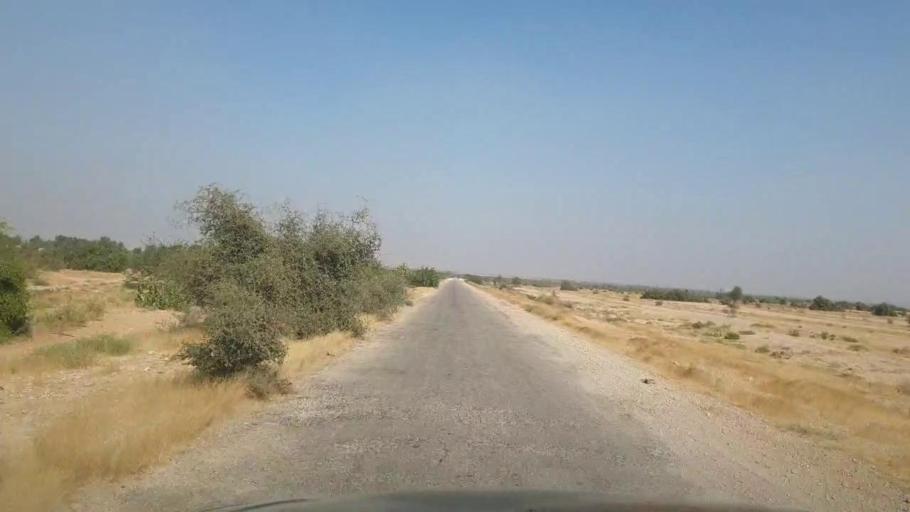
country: PK
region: Sindh
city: Jamshoro
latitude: 25.4695
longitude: 67.8150
